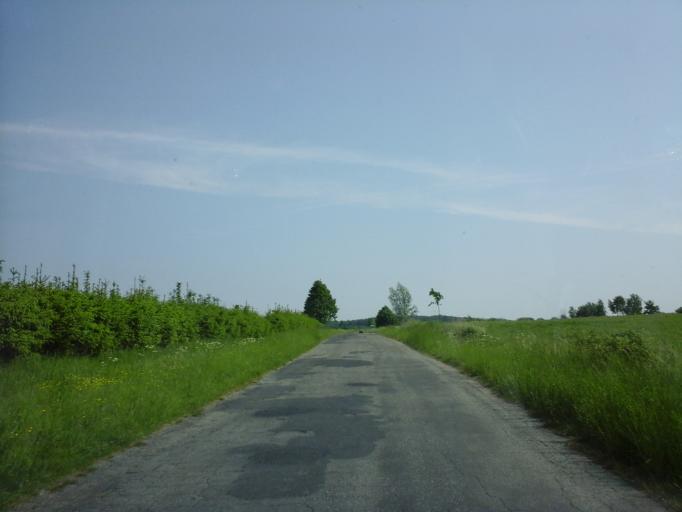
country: PL
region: West Pomeranian Voivodeship
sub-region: Powiat stargardzki
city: Dobrzany
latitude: 53.3607
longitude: 15.4396
